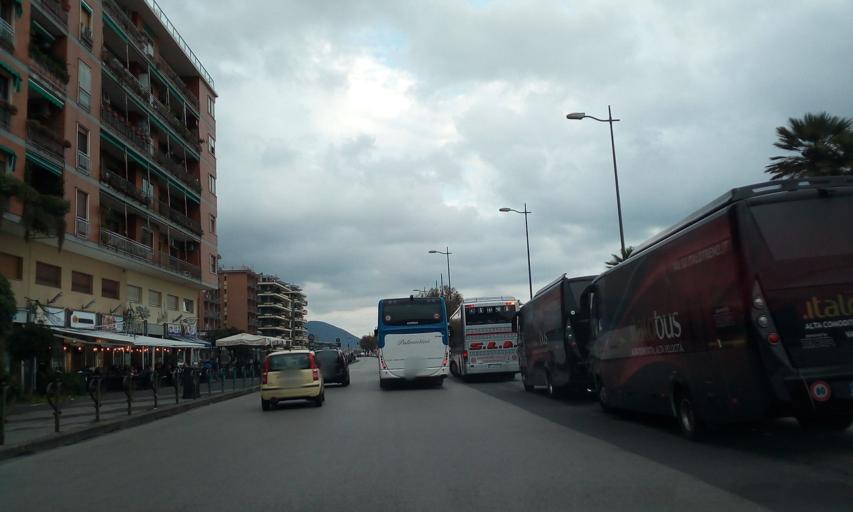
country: IT
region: Campania
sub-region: Provincia di Salerno
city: Salerno
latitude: 40.6740
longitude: 14.7701
